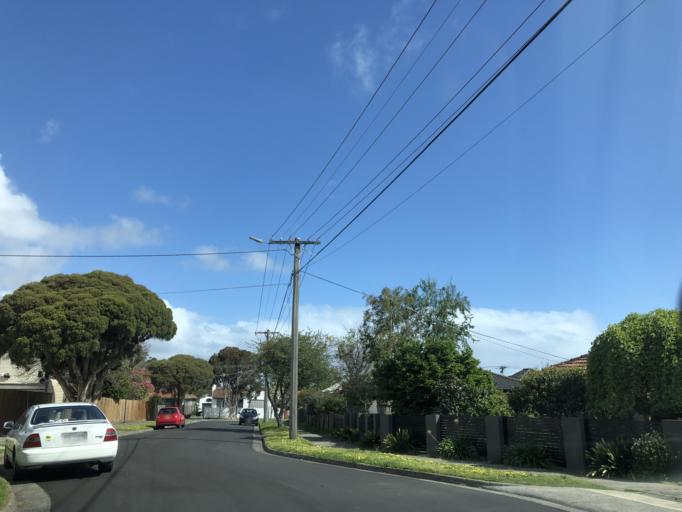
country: AU
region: Victoria
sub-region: Kingston
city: Clayton South
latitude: -37.9290
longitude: 145.1123
